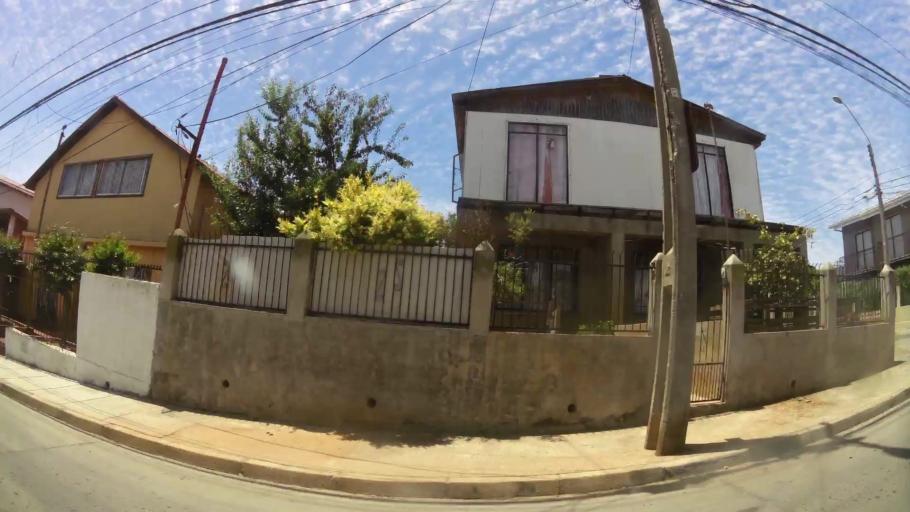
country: CL
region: Valparaiso
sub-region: Provincia de Valparaiso
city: Vina del Mar
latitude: -33.0466
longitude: -71.5796
